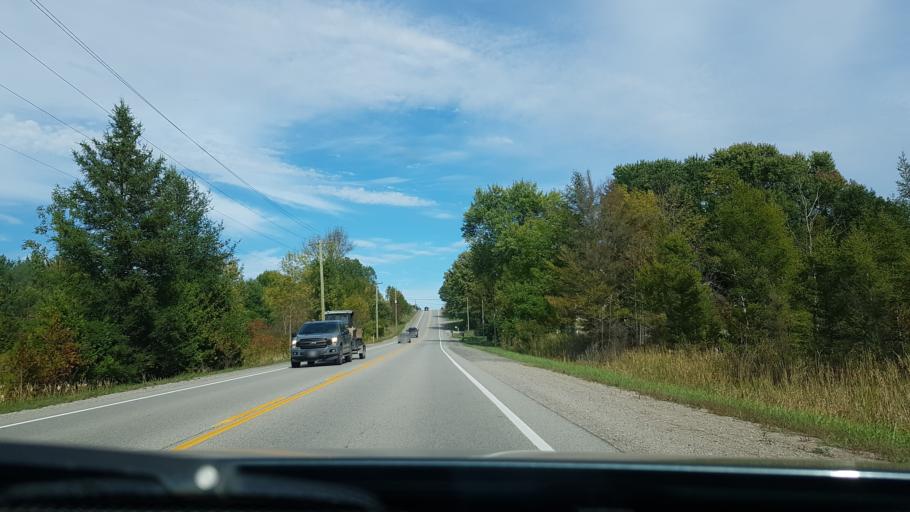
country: CA
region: Ontario
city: Angus
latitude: 44.4815
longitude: -79.8315
